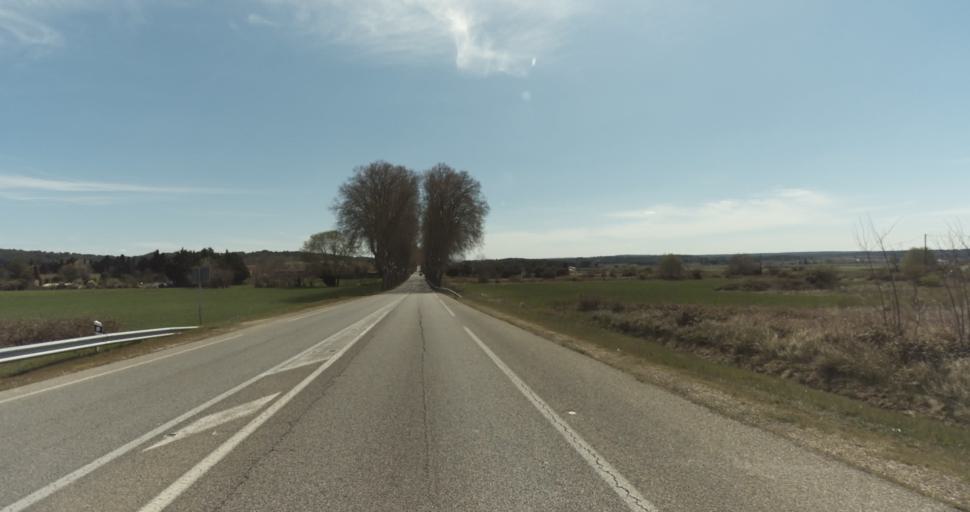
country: FR
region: Provence-Alpes-Cote d'Azur
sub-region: Departement des Bouches-du-Rhone
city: Lambesc
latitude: 43.6374
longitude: 5.2784
